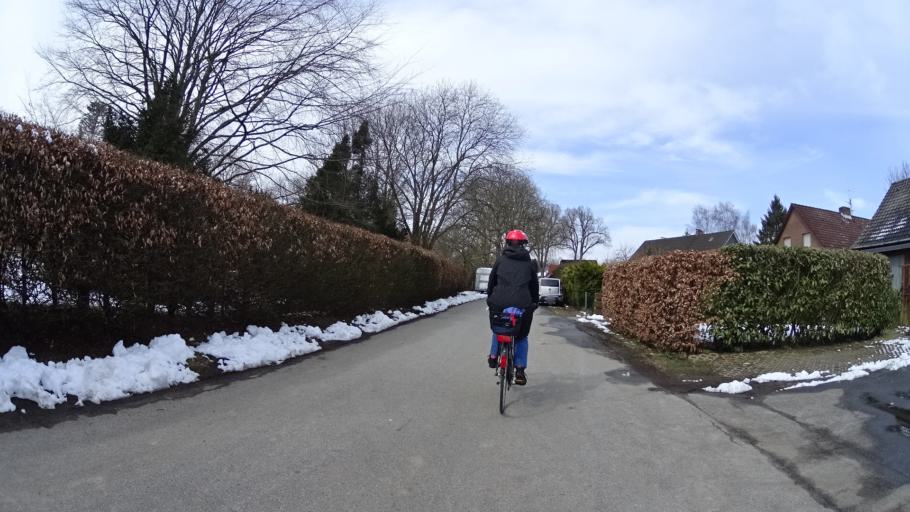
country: DE
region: Schleswig-Holstein
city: Loptin
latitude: 54.1737
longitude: 10.2187
